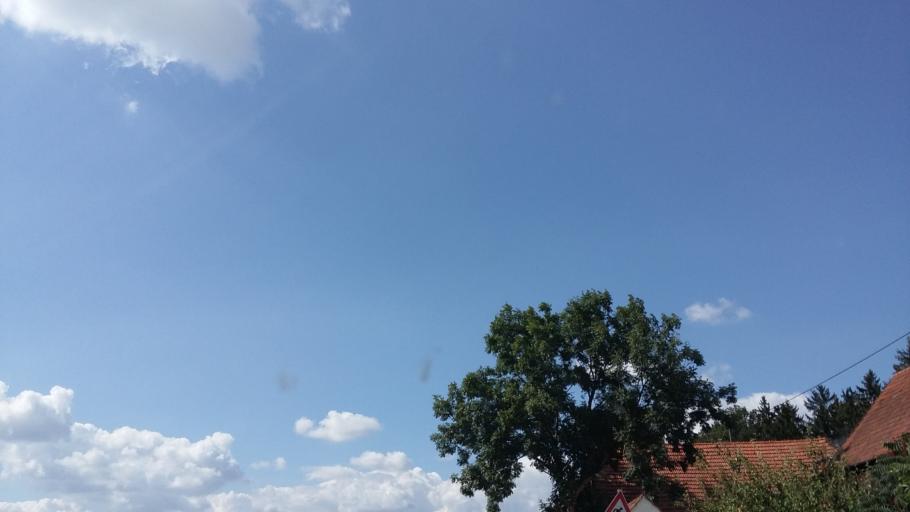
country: DE
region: Bavaria
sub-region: Swabia
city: Holzheim
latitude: 48.3515
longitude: 10.1190
